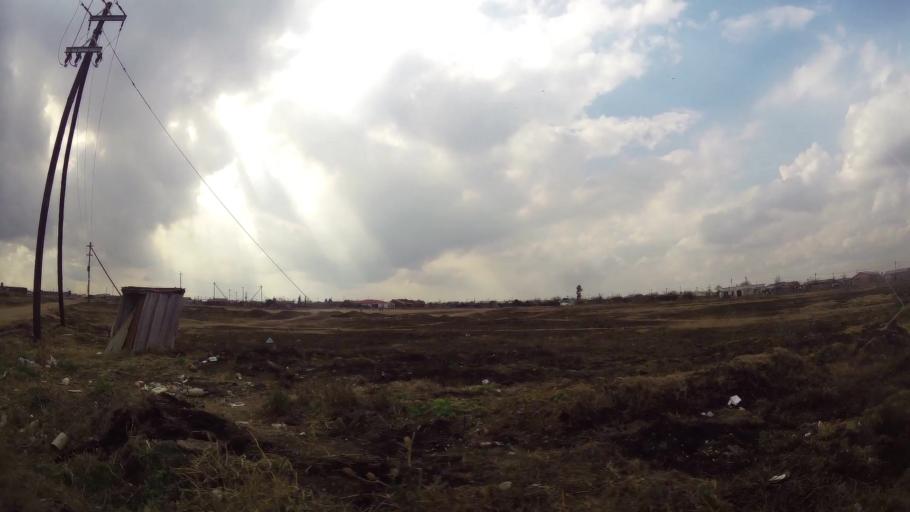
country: ZA
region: Orange Free State
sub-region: Fezile Dabi District Municipality
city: Sasolburg
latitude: -26.8642
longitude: 27.8978
